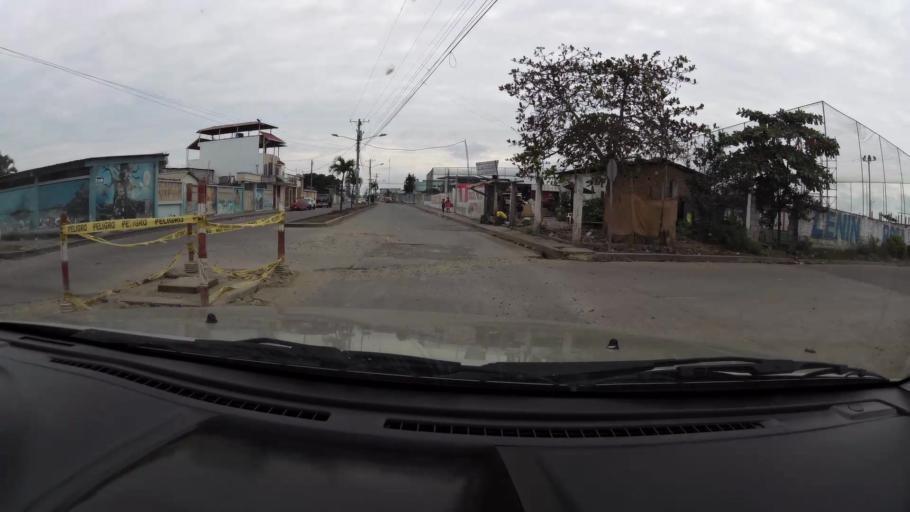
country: EC
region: El Oro
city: Machala
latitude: -3.2474
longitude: -79.9554
